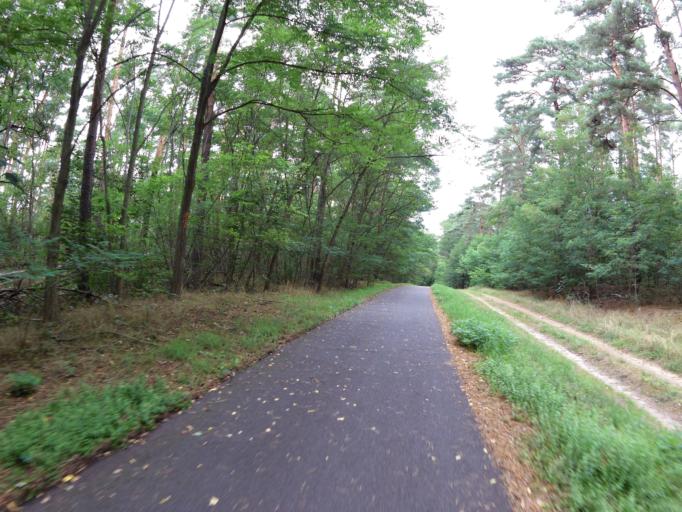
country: DE
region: Brandenburg
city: Reichenwalde
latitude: 52.2427
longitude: 13.9810
